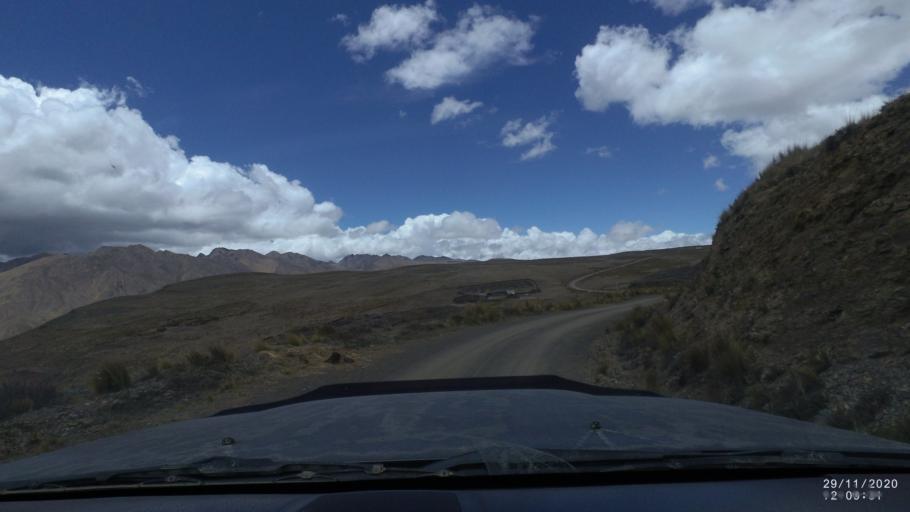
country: BO
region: Cochabamba
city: Cochabamba
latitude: -17.1305
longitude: -66.3043
